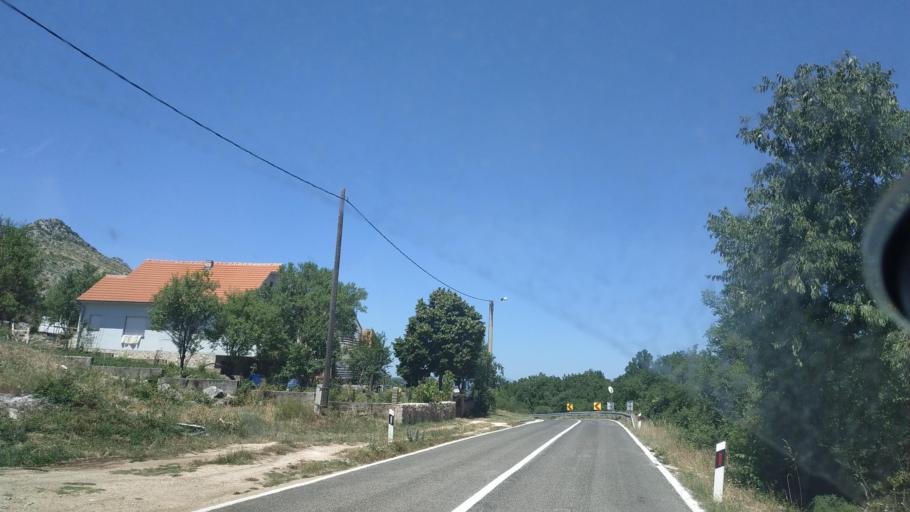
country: HR
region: Sibensko-Kniniska
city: Drnis
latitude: 43.8983
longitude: 16.2105
